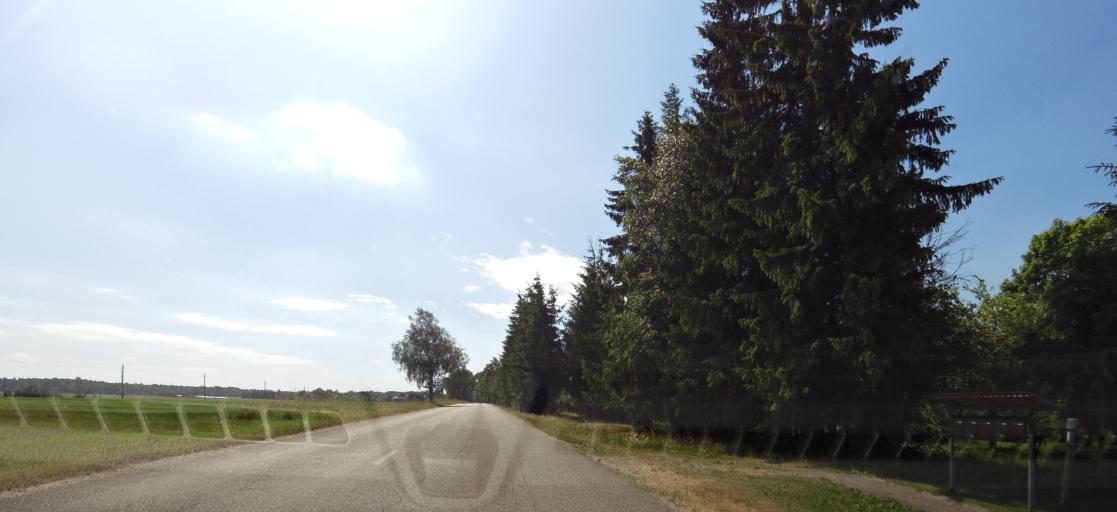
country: LT
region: Panevezys
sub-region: Birzai
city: Birzai
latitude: 56.1995
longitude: 24.9224
